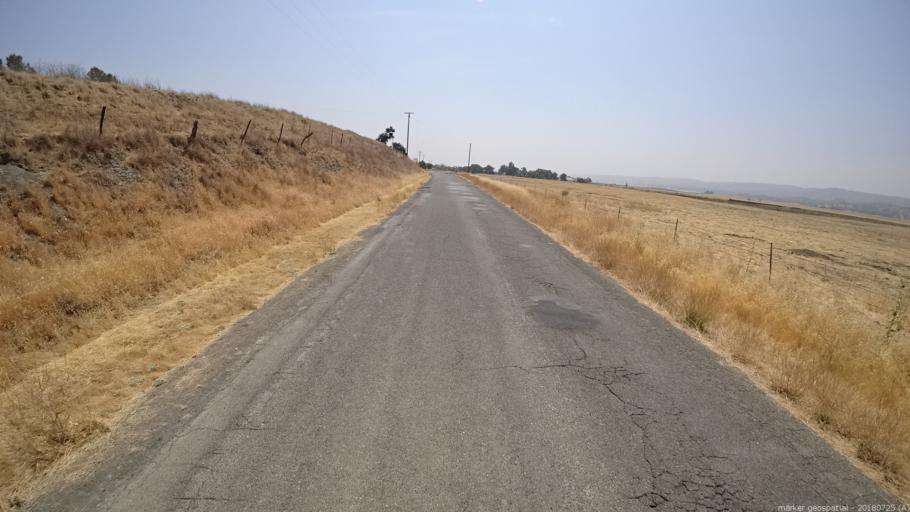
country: US
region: California
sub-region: San Luis Obispo County
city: Shandon
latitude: 35.8501
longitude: -120.3829
